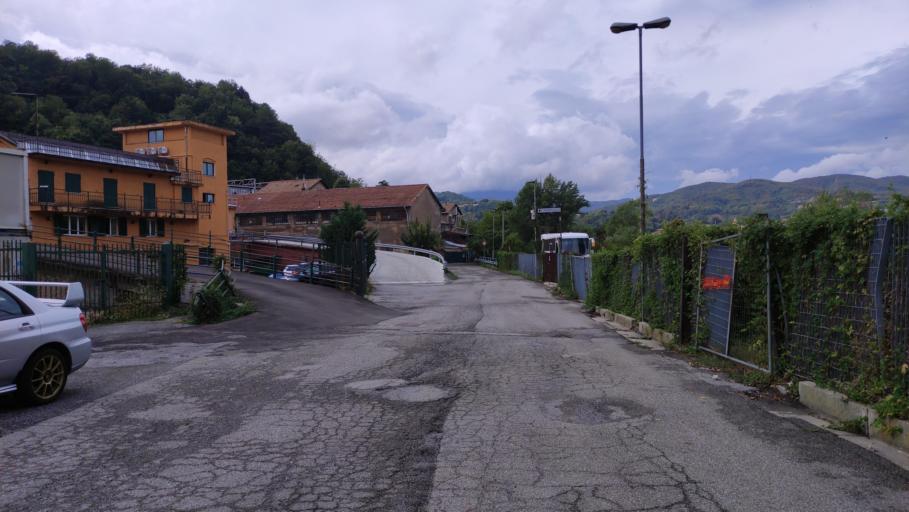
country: IT
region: Liguria
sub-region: Provincia di Genova
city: Busalla
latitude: 44.5683
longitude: 8.9622
